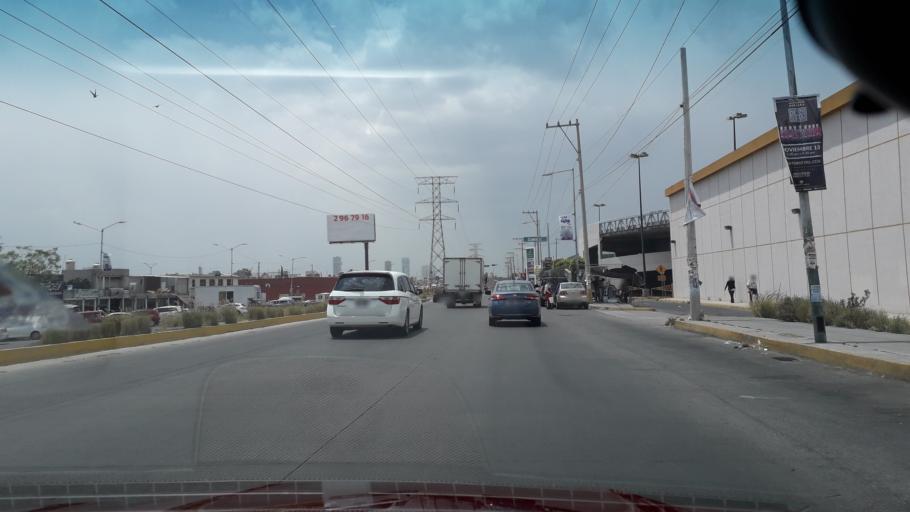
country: MX
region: Puebla
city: Tlazcalancingo
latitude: 19.0052
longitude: -98.2392
